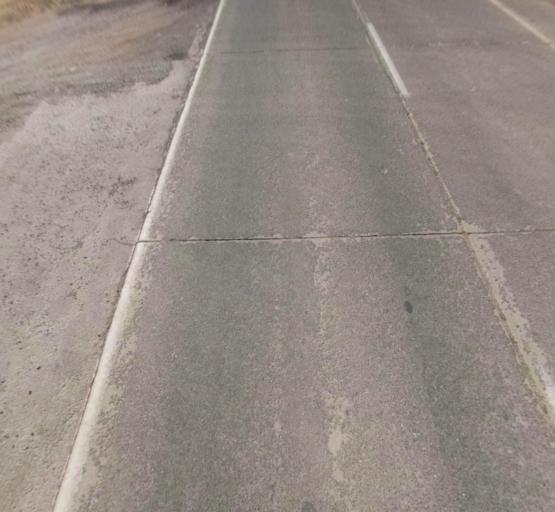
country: US
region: California
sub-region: Madera County
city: Chowchilla
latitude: 37.1378
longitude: -120.2724
